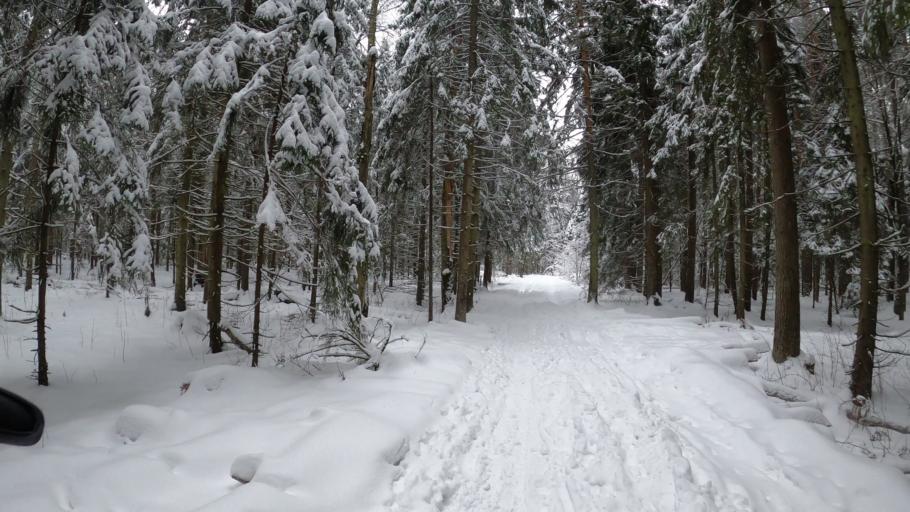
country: RU
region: Moskovskaya
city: Firsanovka
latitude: 55.9577
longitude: 37.2219
